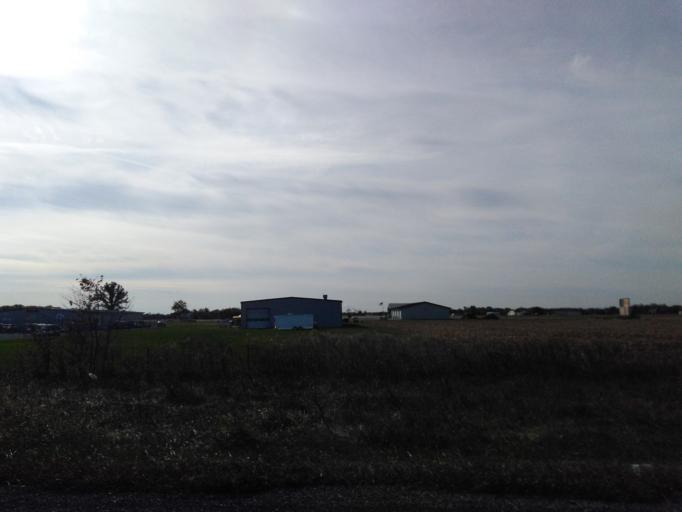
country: US
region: Illinois
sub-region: Madison County
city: Highland
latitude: 38.7862
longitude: -89.6380
